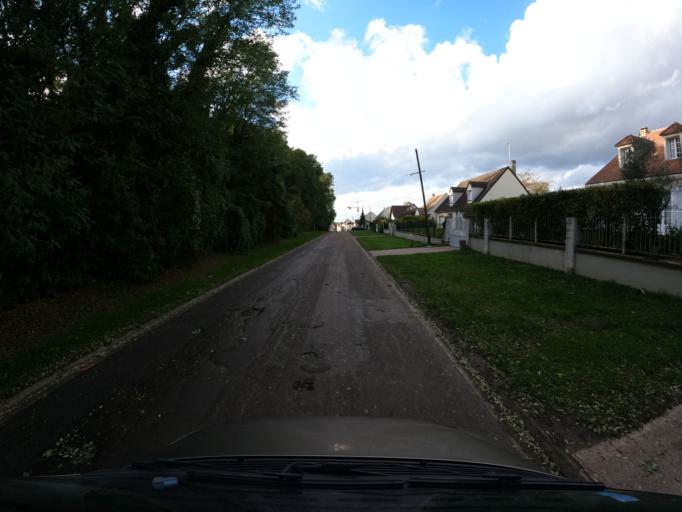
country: FR
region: Ile-de-France
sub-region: Departement de Seine-et-Marne
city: Chalifert
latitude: 48.8870
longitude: 2.7766
